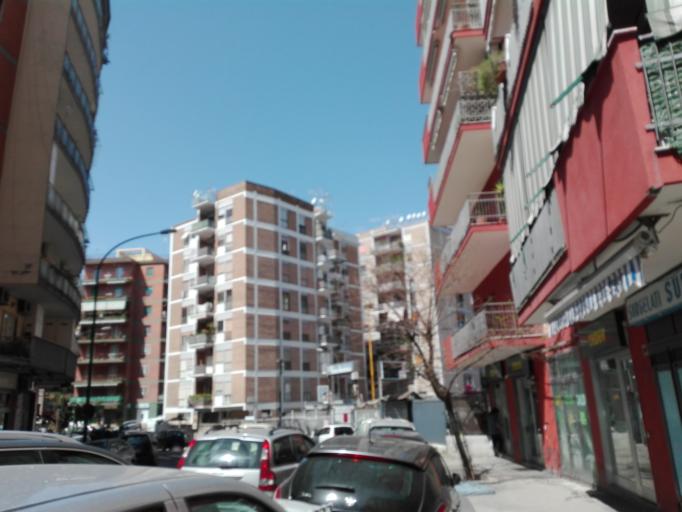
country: IT
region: Campania
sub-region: Provincia di Napoli
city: Napoli
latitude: 40.8514
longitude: 14.2227
